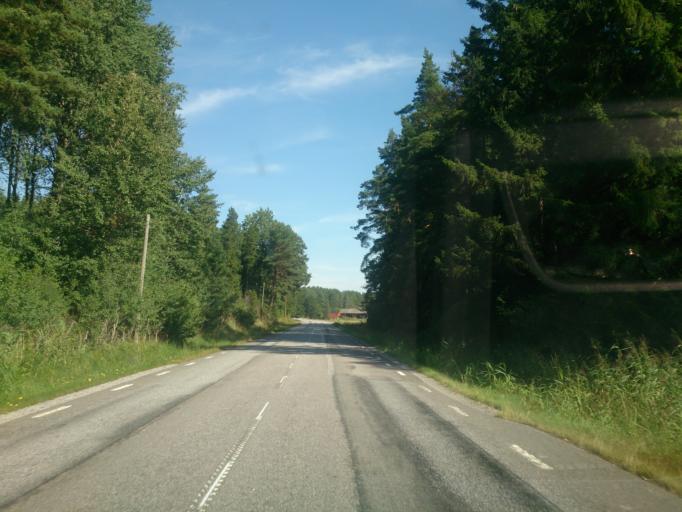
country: SE
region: OEstergoetland
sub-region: Norrkopings Kommun
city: Norrkoping
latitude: 58.4876
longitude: 16.1039
